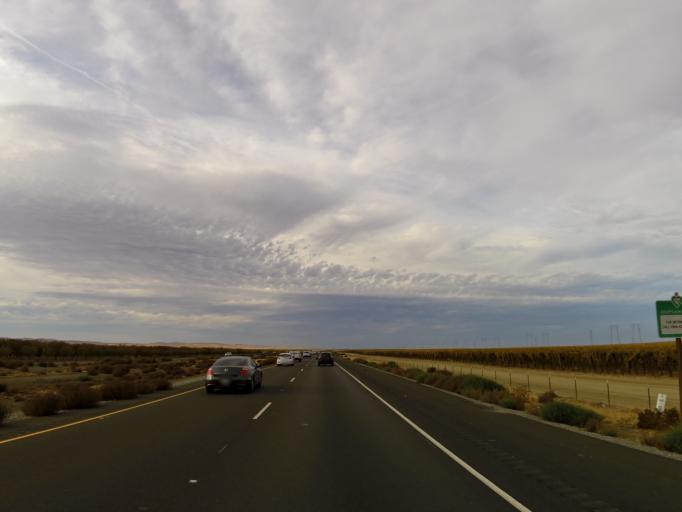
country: US
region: California
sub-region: Kings County
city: Kettleman City
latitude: 35.9081
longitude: -119.8848
